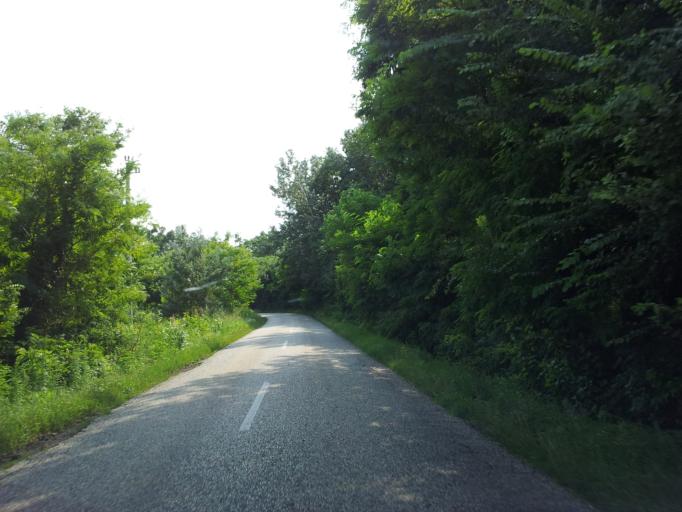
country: HU
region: Pest
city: Szigetujfalu
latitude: 47.2069
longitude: 18.9132
